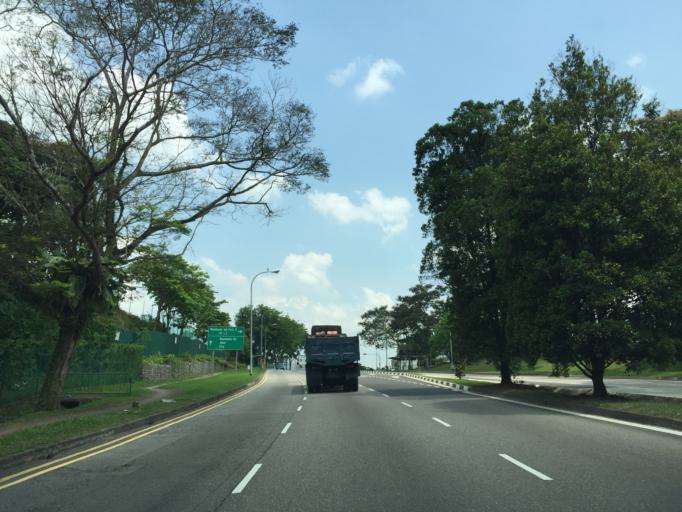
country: MY
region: Johor
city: Johor Bahru
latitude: 1.4302
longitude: 103.7674
